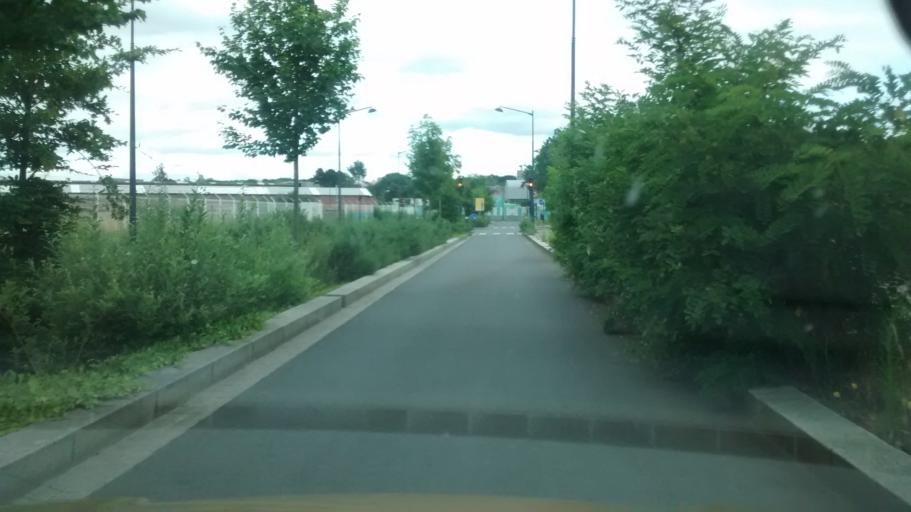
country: FR
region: Brittany
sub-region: Departement d'Ille-et-Vilaine
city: Rennes
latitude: 48.0987
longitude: -1.7045
